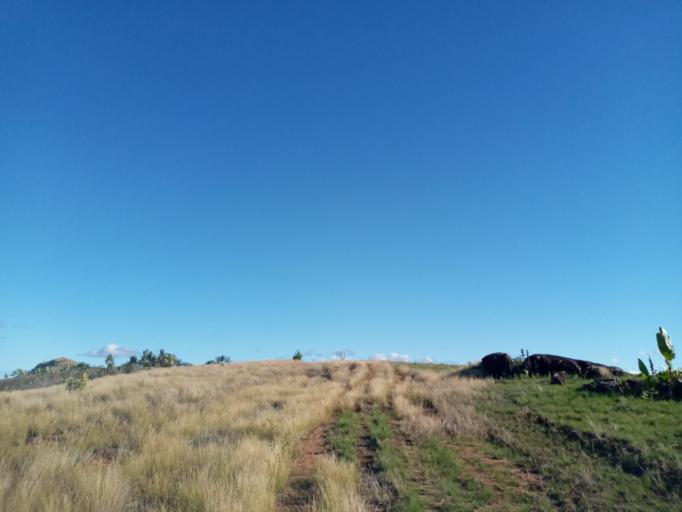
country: MG
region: Anosy
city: Fort Dauphin
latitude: -24.4061
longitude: 47.2551
